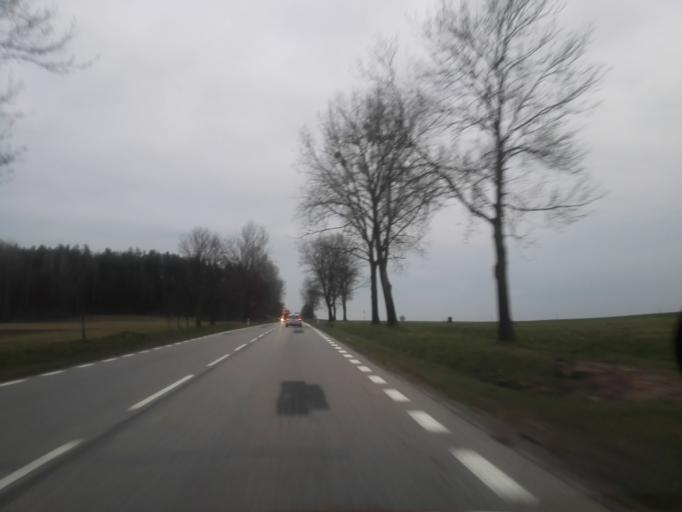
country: PL
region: Podlasie
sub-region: Powiat lomzynski
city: Piatnica
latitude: 53.2698
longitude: 22.1308
